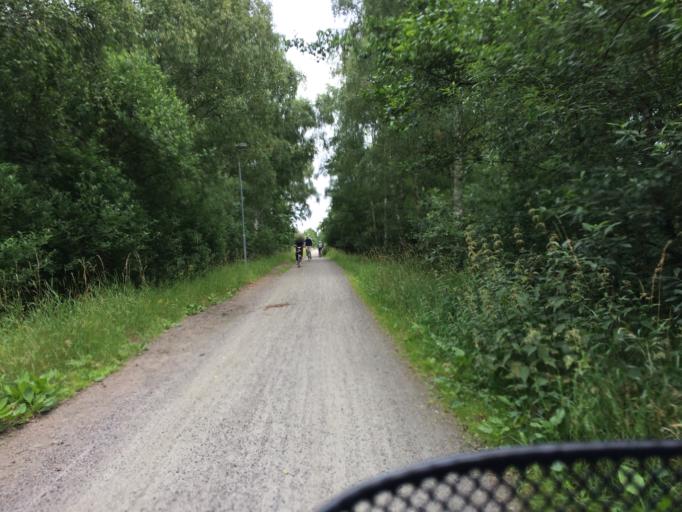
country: SE
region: Skane
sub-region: Vellinge Kommun
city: Skanor med Falsterbo
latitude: 55.4085
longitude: 12.8785
